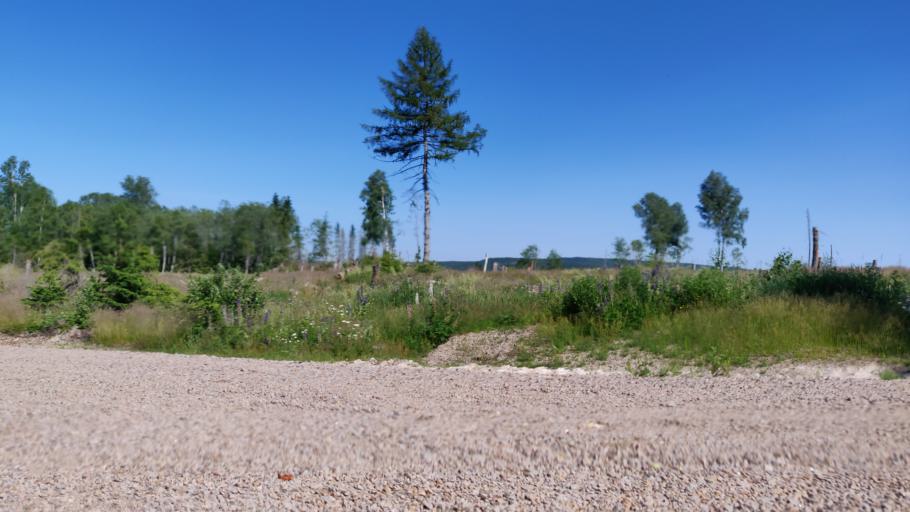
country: SE
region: Vaermland
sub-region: Hagfors Kommun
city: Hagfors
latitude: 59.9704
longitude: 13.6090
